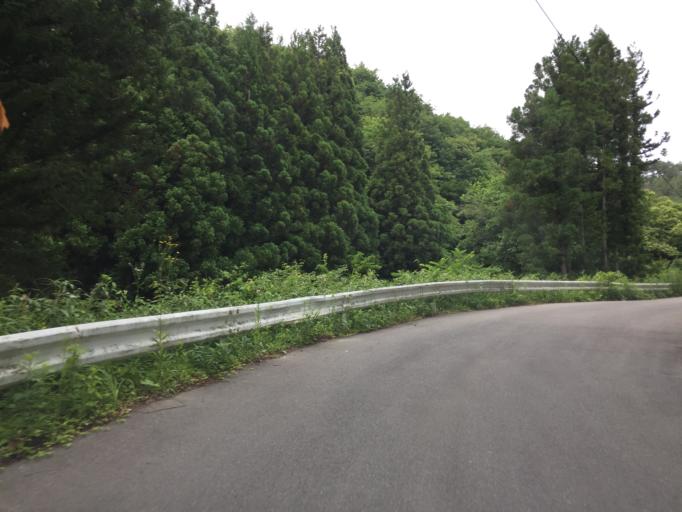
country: JP
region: Fukushima
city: Funehikimachi-funehiki
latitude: 37.4422
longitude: 140.7778
